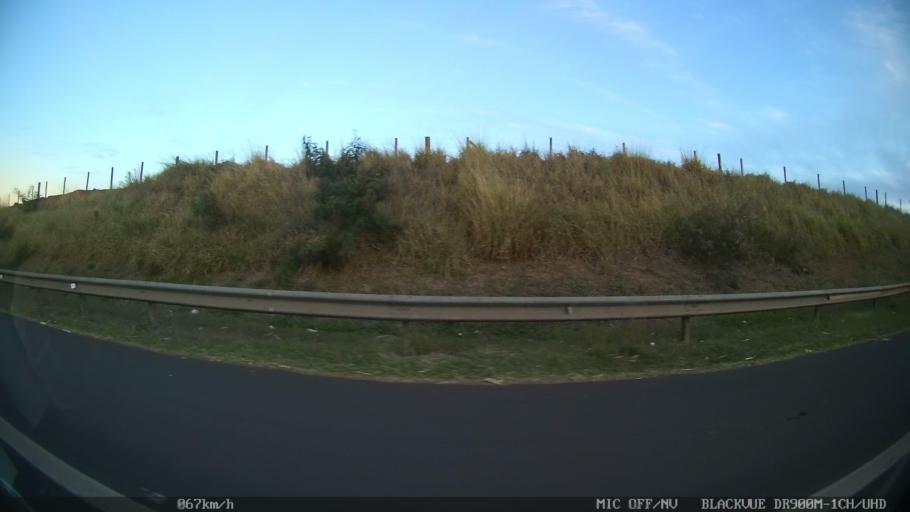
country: BR
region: Sao Paulo
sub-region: Catanduva
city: Catanduva
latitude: -21.1312
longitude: -49.0145
